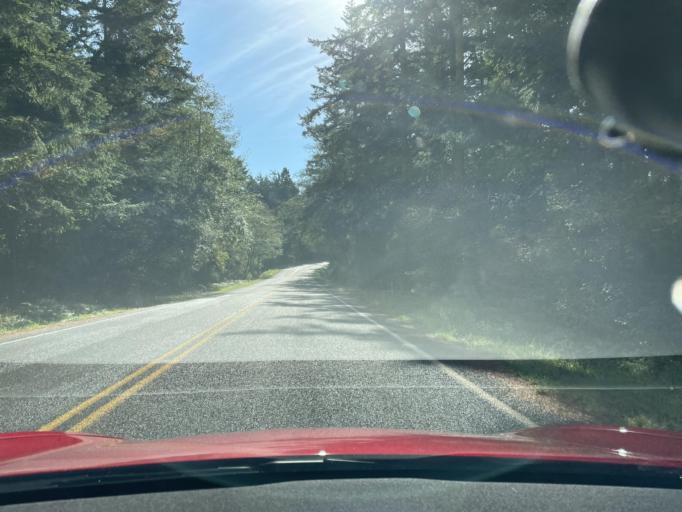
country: US
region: Washington
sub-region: San Juan County
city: Friday Harbor
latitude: 48.4693
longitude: -123.0317
